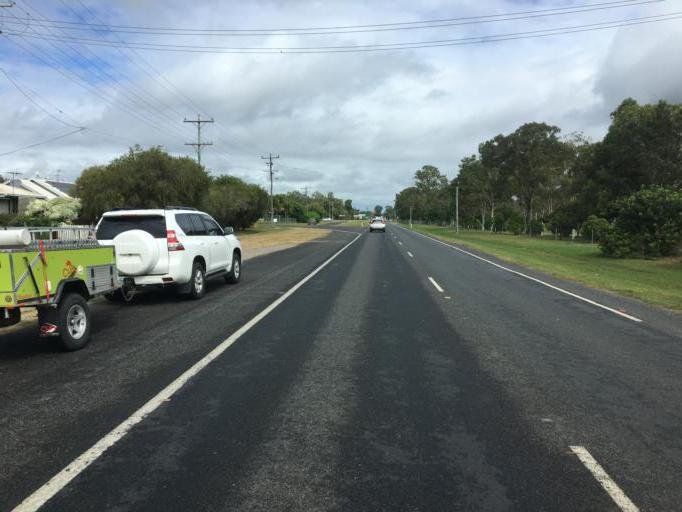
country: AU
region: Queensland
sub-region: Tablelands
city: Mareeba
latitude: -16.9860
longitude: 145.4167
